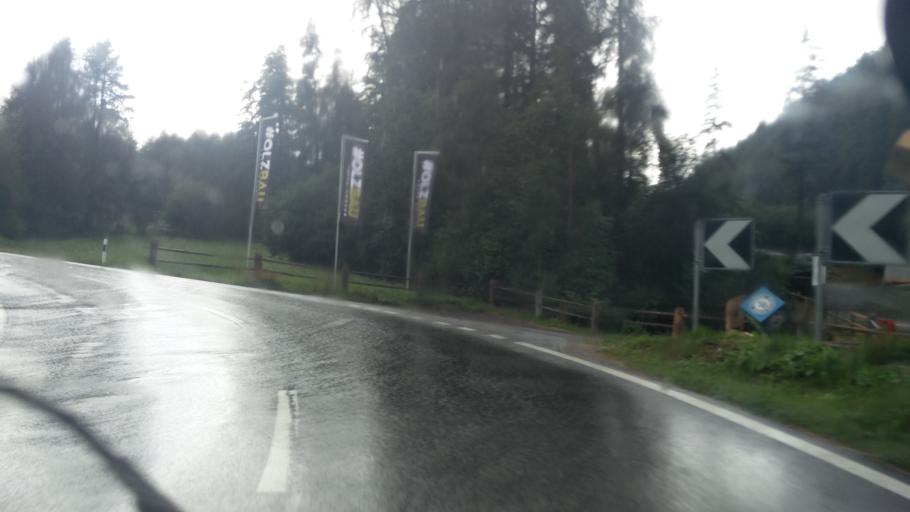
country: IT
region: Trentino-Alto Adige
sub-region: Bolzano
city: Tubre
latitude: 46.6026
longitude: 10.3987
